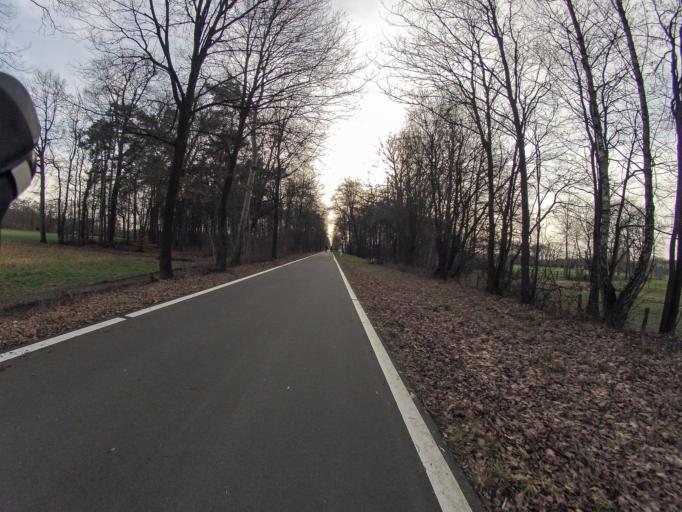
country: DE
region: North Rhine-Westphalia
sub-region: Regierungsbezirk Munster
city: Neuenkirchen
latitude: 52.2019
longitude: 7.3946
